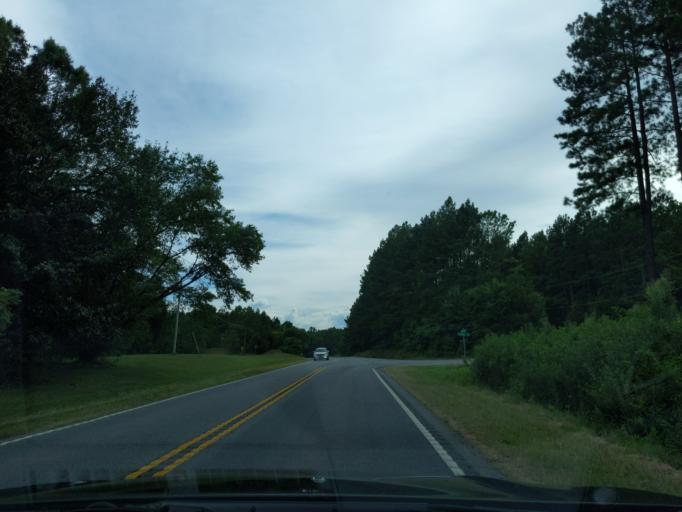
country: US
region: North Carolina
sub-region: Cabarrus County
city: Mount Pleasant
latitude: 35.4228
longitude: -80.4176
